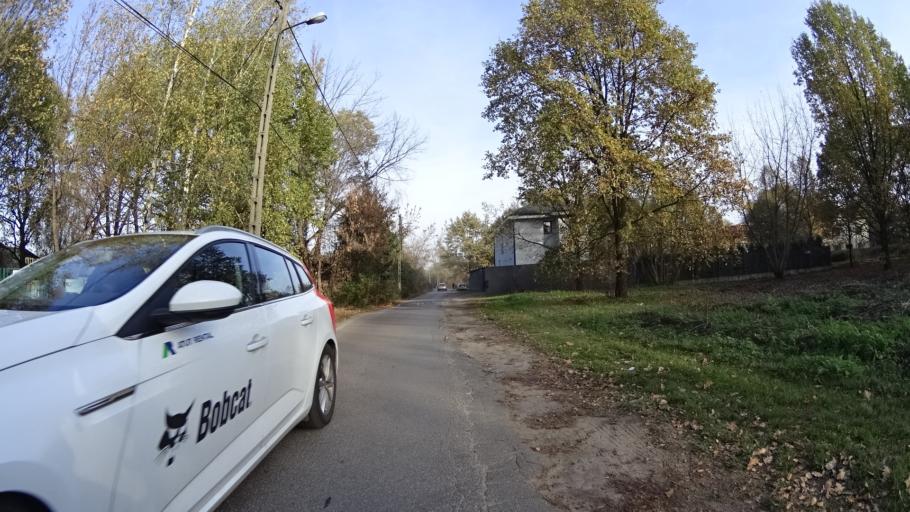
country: PL
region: Masovian Voivodeship
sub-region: Powiat warszawski zachodni
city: Lomianki
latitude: 52.2945
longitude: 20.8833
